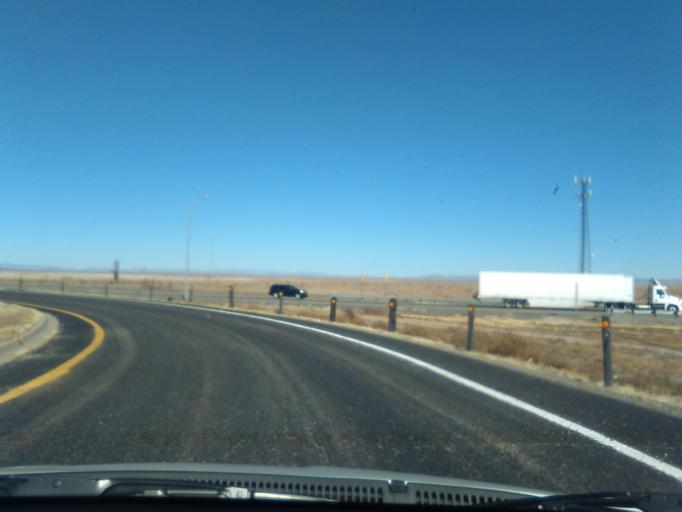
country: US
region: New Mexico
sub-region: Hidalgo County
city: Lordsburg
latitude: 32.3524
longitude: -108.7422
